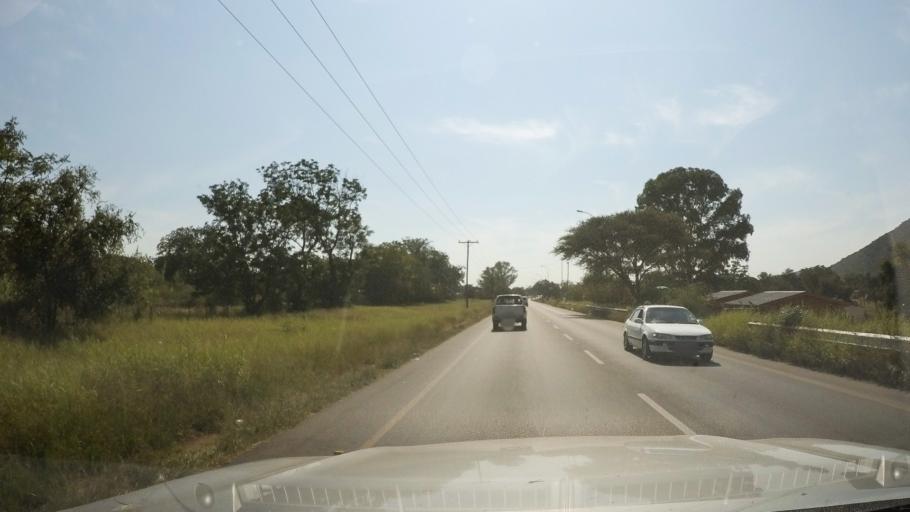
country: BW
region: South East
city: Lobatse
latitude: -25.2189
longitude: 25.6803
